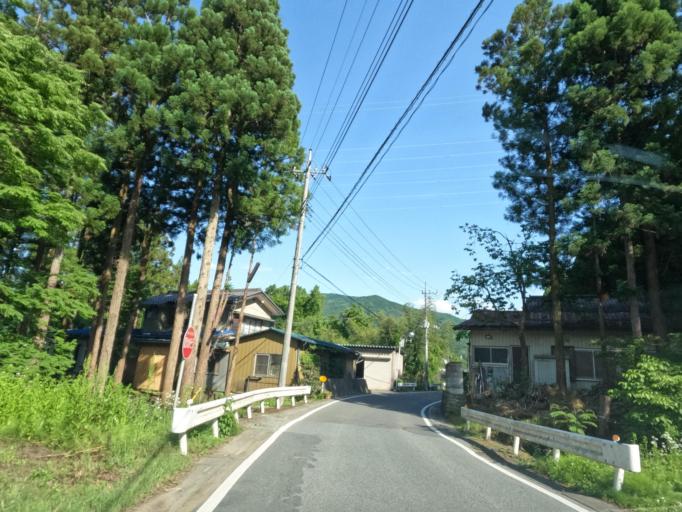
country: JP
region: Saitama
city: Chichibu
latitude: 36.0164
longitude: 139.1069
